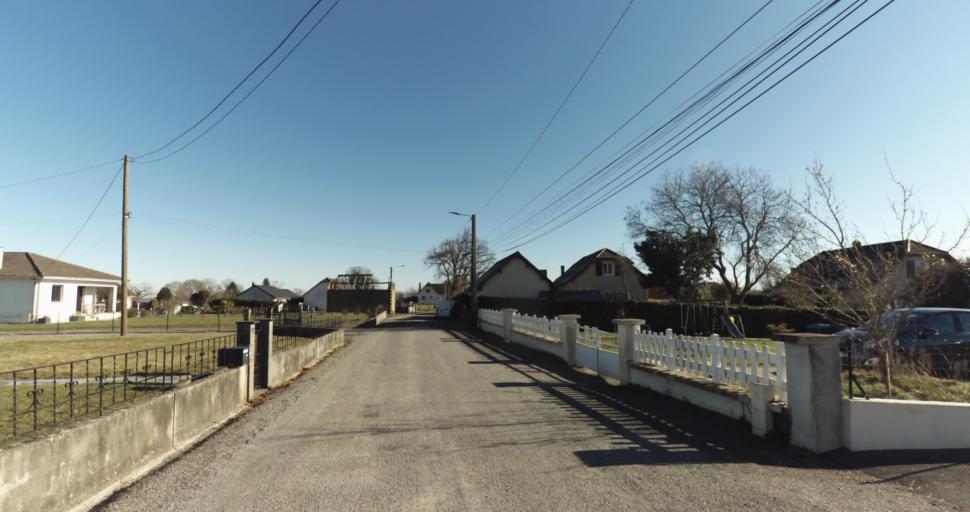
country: FR
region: Aquitaine
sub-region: Departement des Pyrenees-Atlantiques
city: Morlaas
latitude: 43.3386
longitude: -0.2751
